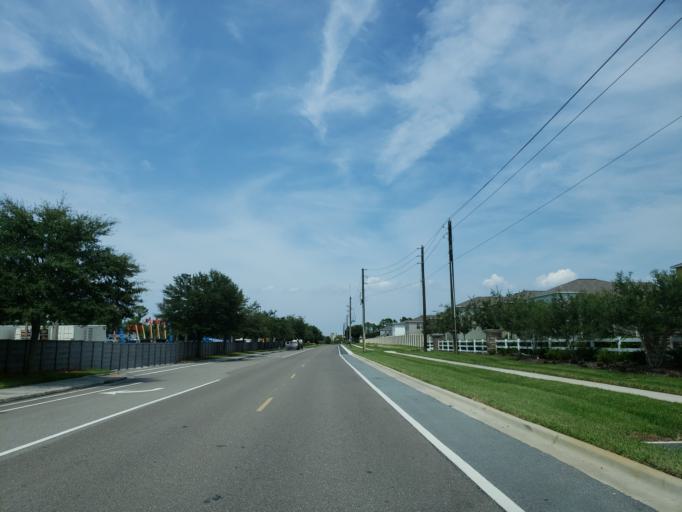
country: US
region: Florida
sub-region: Hillsborough County
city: Riverview
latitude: 27.8491
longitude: -82.3433
